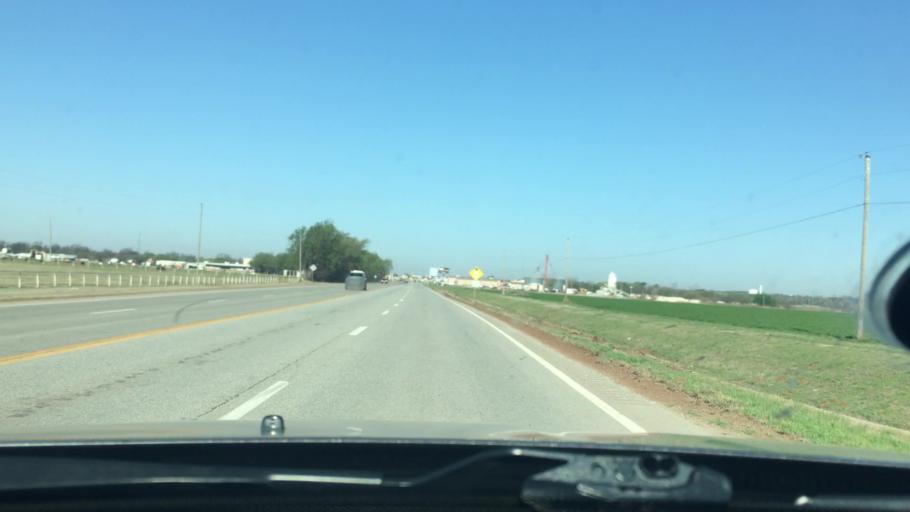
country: US
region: Oklahoma
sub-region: Garvin County
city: Lindsay
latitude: 34.8355
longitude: -97.5870
